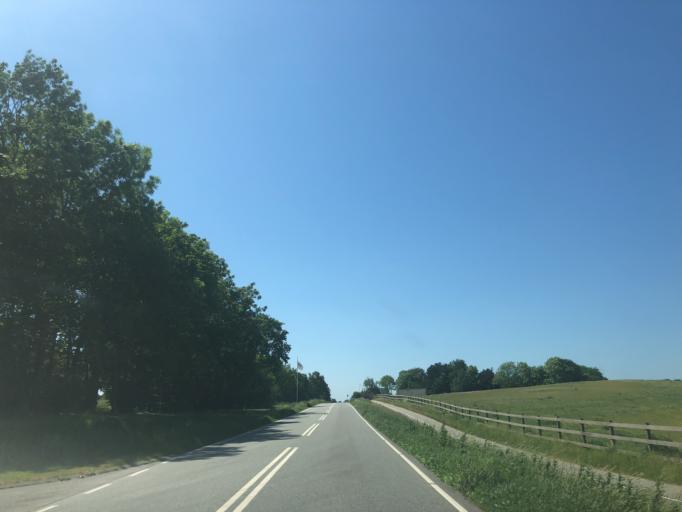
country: DK
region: Capital Region
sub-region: Gribskov Kommune
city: Graested
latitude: 56.0535
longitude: 12.2586
